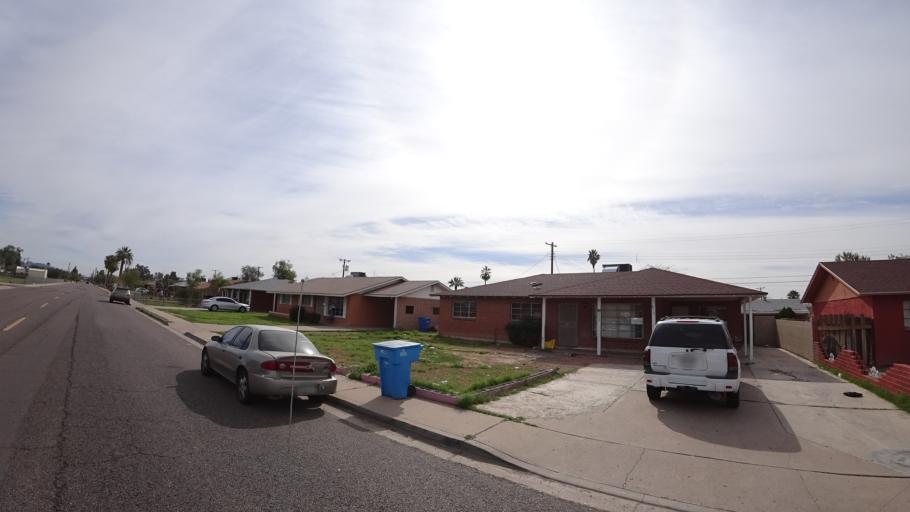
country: US
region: Arizona
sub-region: Maricopa County
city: Glendale
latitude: 33.5313
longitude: -112.1244
